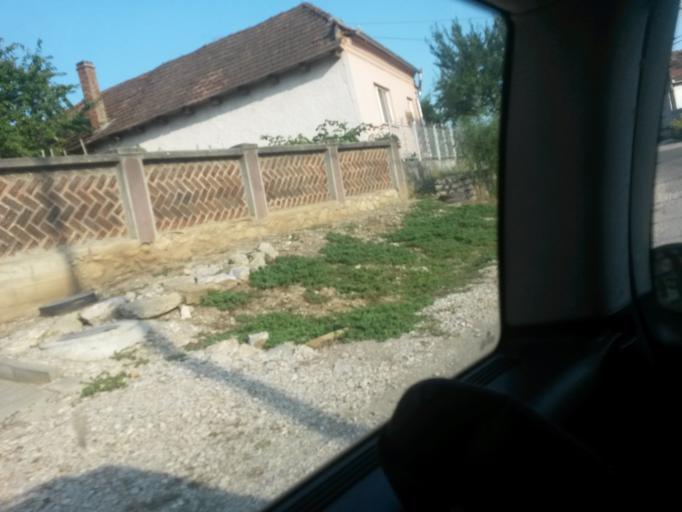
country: RO
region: Alba
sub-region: Municipiul Aiud
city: Aiudul de Sus
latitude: 46.3197
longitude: 23.6856
